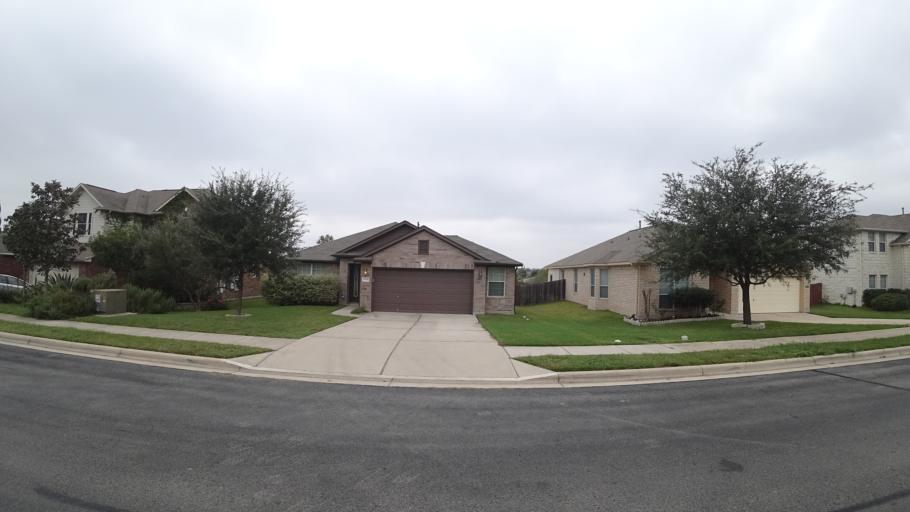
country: US
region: Texas
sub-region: Travis County
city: Pflugerville
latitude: 30.3736
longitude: -97.6526
